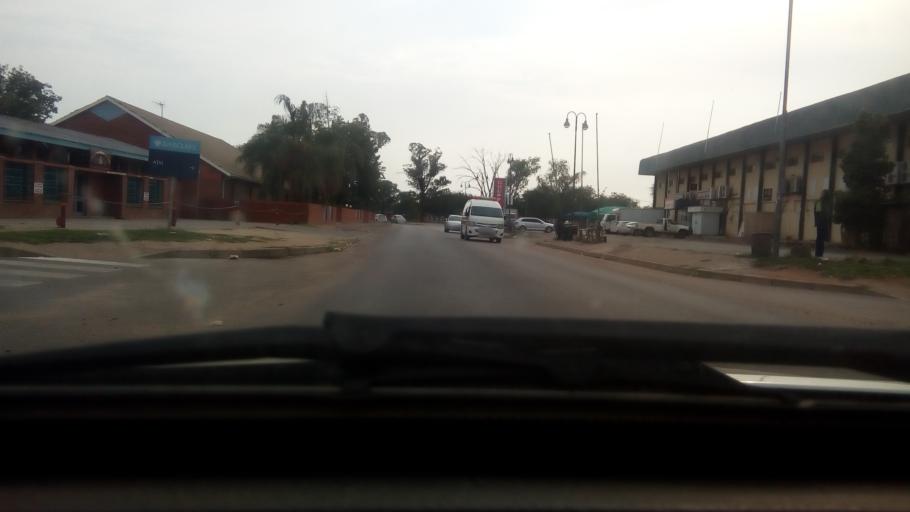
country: BW
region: South East
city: Gaborone
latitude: -24.6673
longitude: 25.9395
